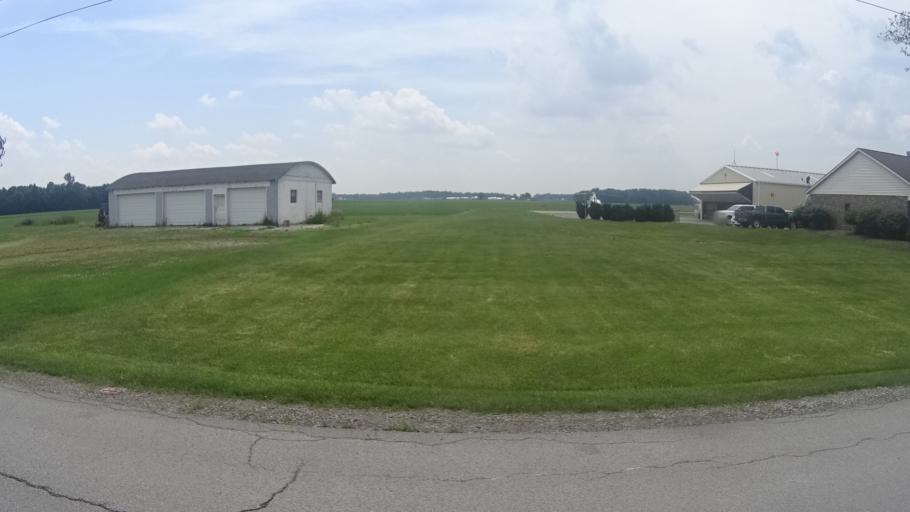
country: US
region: Ohio
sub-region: Erie County
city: Milan
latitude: 41.3153
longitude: -82.6102
